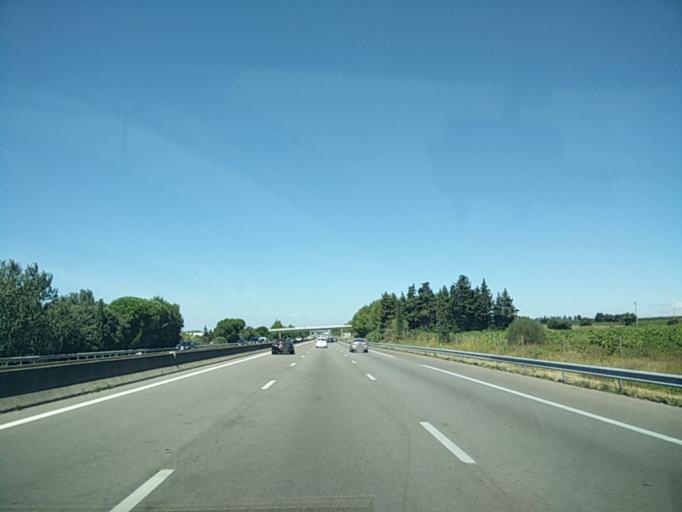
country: FR
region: Provence-Alpes-Cote d'Azur
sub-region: Departement du Vaucluse
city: Morieres-les-Avignon
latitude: 43.9554
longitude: 4.9058
